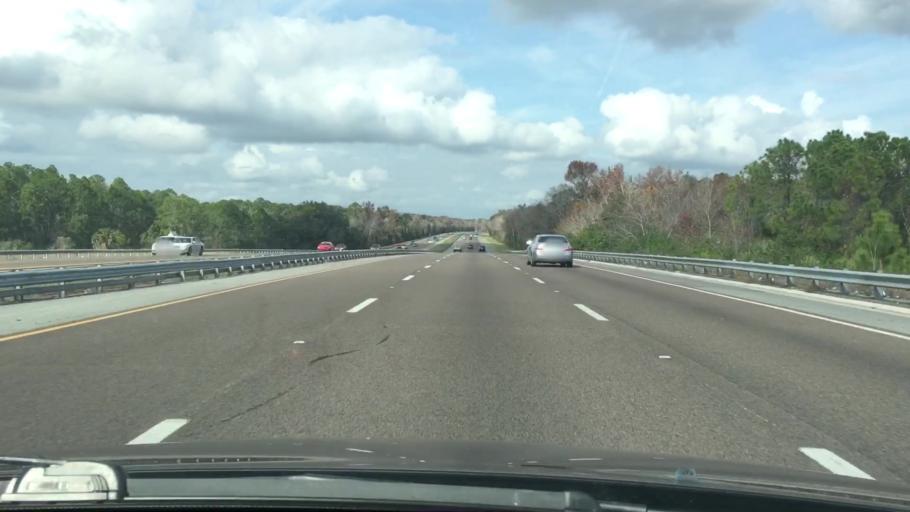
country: US
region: Florida
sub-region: Volusia County
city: Oak Hill
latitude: 28.8341
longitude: -80.9121
